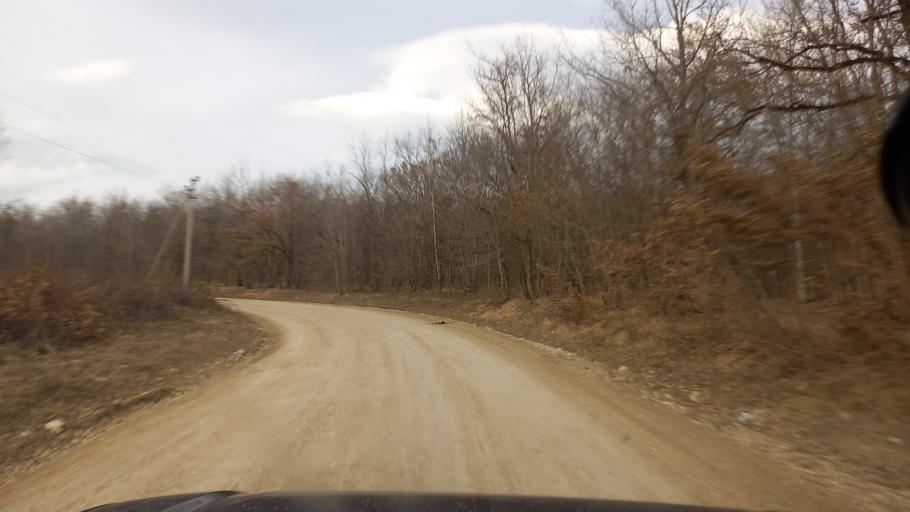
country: RU
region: Adygeya
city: Kamennomostskiy
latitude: 44.1441
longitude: 40.2581
